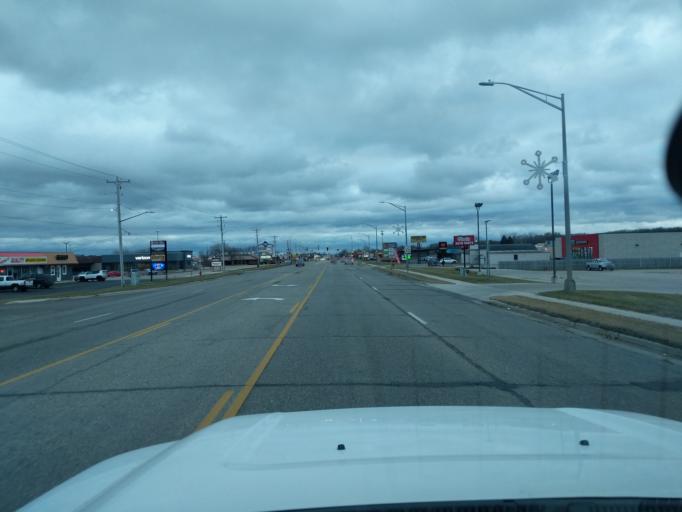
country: US
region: Minnesota
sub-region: Kandiyohi County
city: Willmar
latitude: 45.1078
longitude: -95.0428
